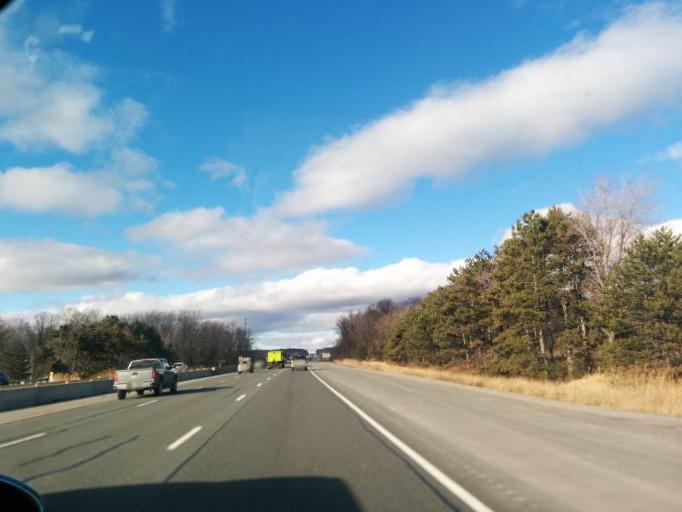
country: CA
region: Ontario
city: Vaughan
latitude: 43.9329
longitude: -79.5688
